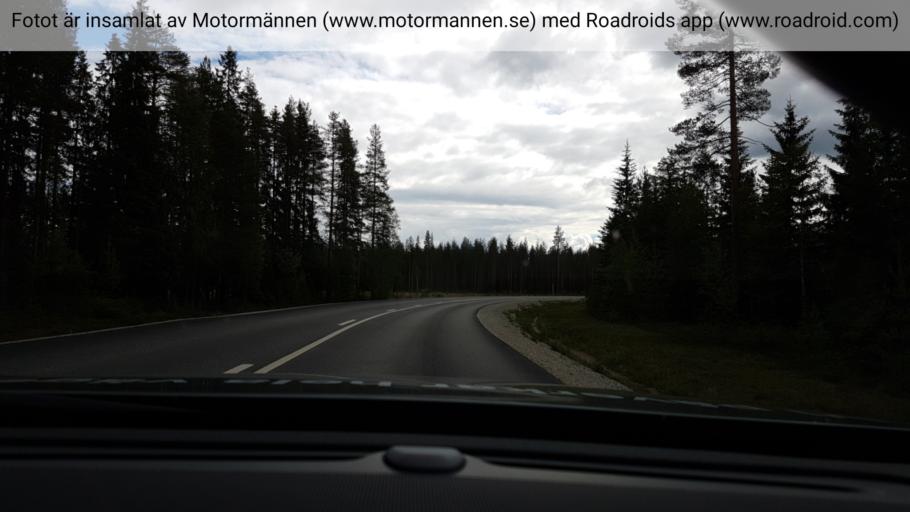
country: SE
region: Vaesterbotten
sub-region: Vindelns Kommun
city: Vindeln
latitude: 64.0818
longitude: 19.6319
